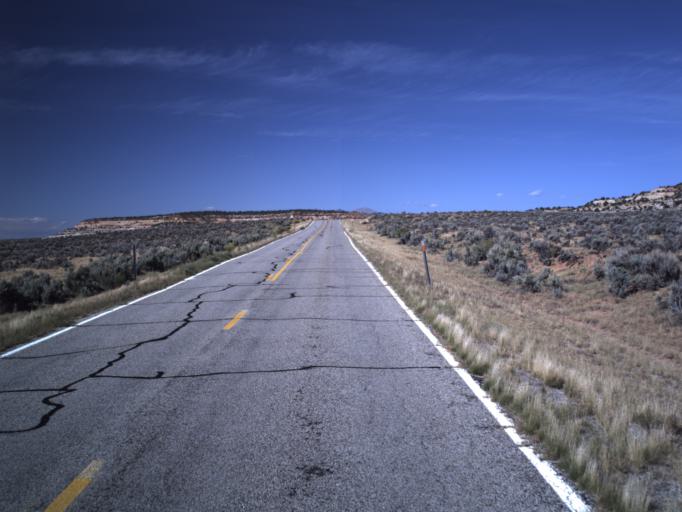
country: US
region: Utah
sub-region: San Juan County
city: Monticello
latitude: 38.0422
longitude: -109.4141
